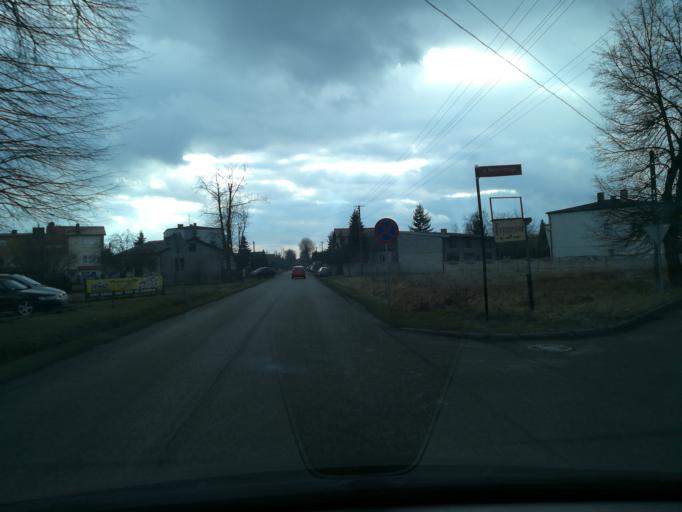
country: PL
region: Lodz Voivodeship
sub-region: Powiat radomszczanski
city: Radomsko
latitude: 51.0596
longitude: 19.4225
